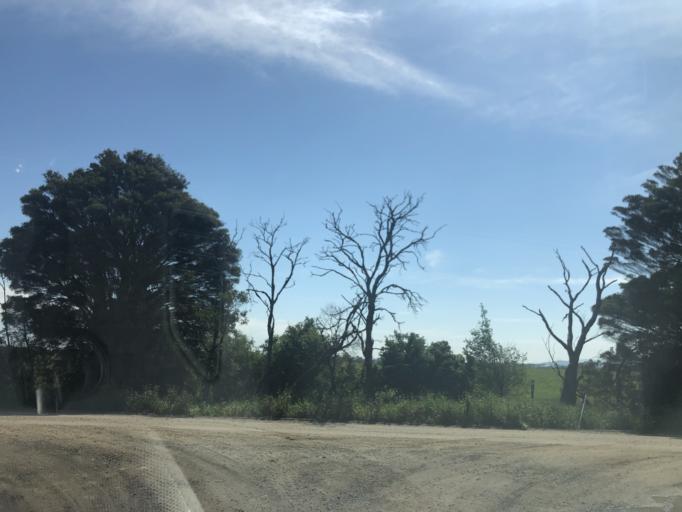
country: AU
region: Victoria
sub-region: Frankston
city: Sandhurst
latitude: -38.0564
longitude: 145.1894
